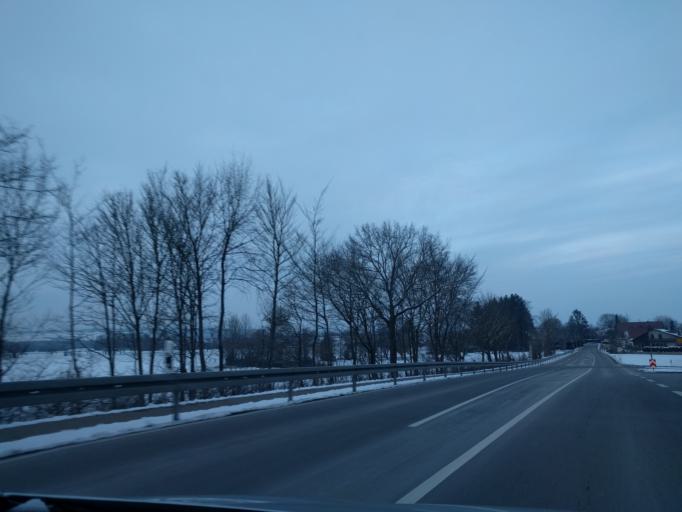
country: DE
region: Bavaria
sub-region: Swabia
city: Rain
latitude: 48.7035
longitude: 10.9073
